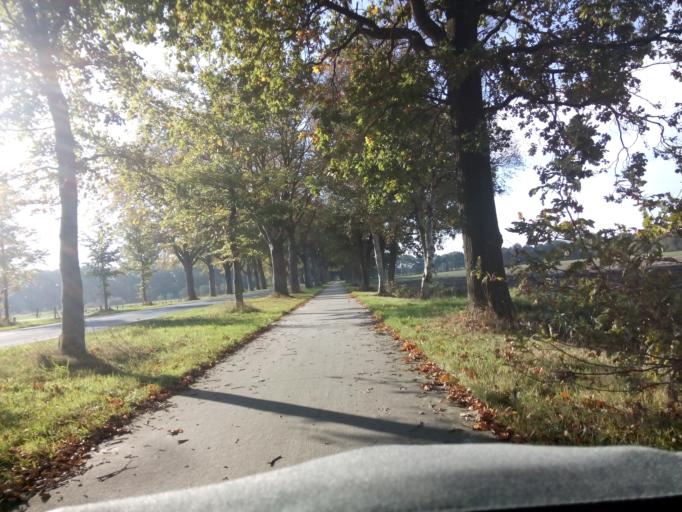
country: NL
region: Drenthe
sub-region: Gemeente Tynaarlo
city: Vries
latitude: 53.0621
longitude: 6.5763
